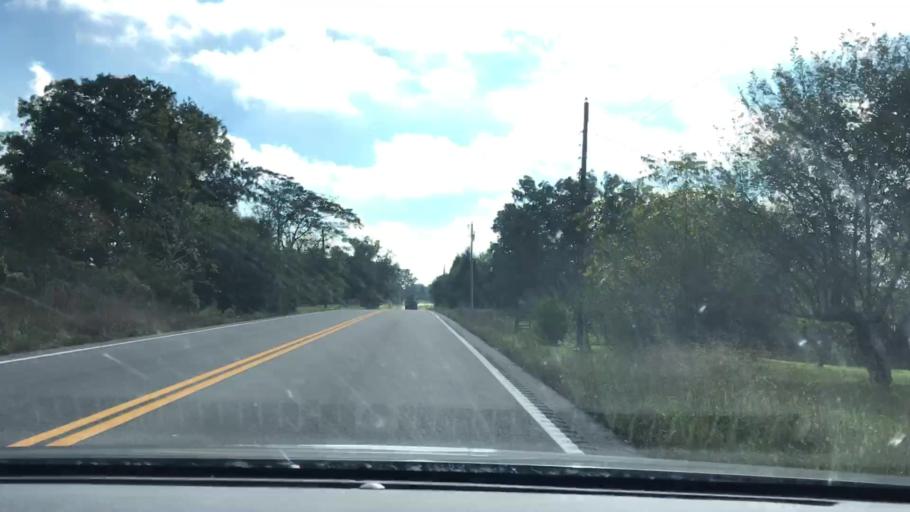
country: US
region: Tennessee
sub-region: Fentress County
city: Grimsley
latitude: 36.1644
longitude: -85.0643
